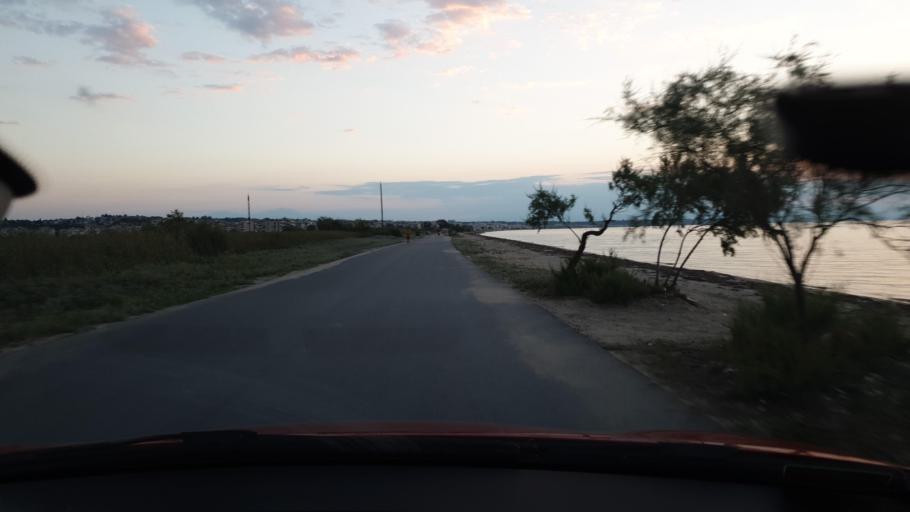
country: GR
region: Central Macedonia
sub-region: Nomos Thessalonikis
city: Peraia
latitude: 40.5162
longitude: 22.9435
